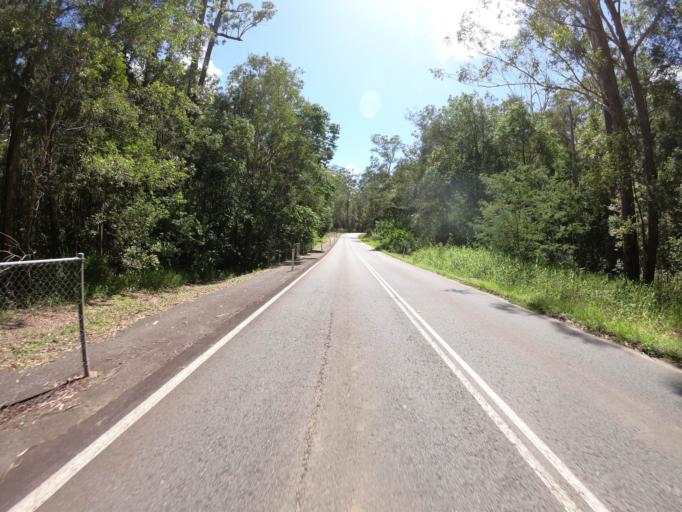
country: AU
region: Queensland
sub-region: Moreton Bay
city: Burpengary
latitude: -27.1489
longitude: 152.9804
